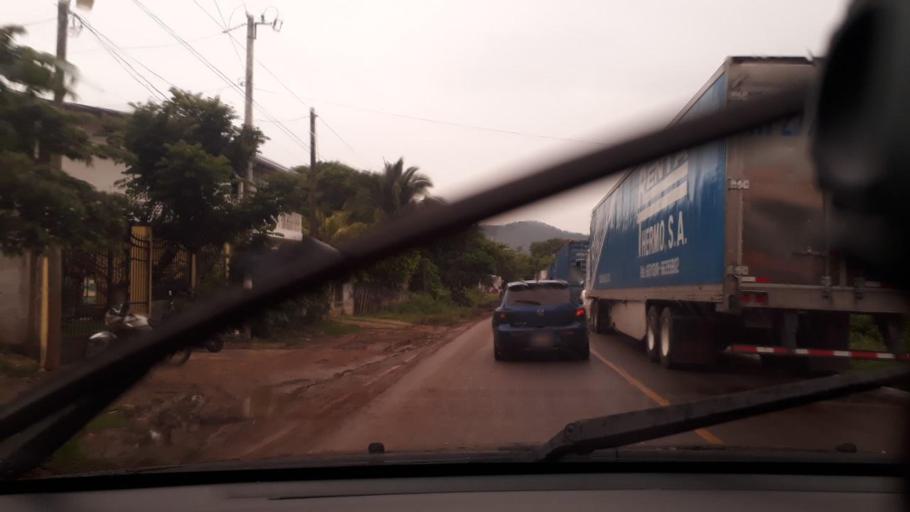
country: GT
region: Jutiapa
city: Atescatempa
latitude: 14.2024
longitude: -89.6803
